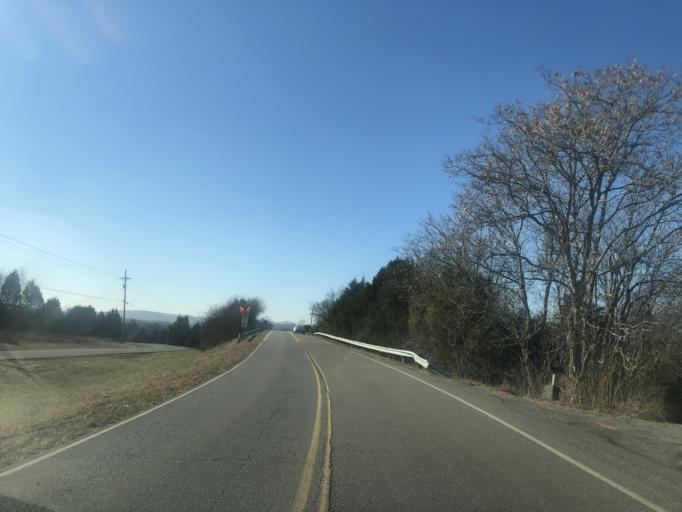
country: US
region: Tennessee
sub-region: Rutherford County
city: Smyrna
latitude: 35.9539
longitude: -86.5501
